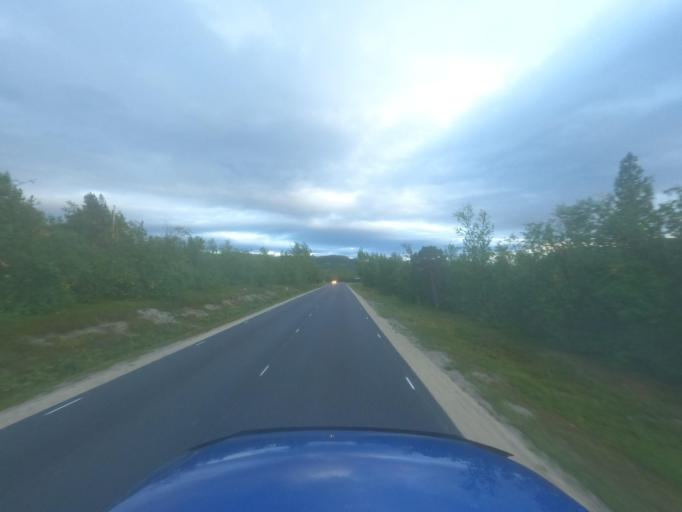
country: NO
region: Finnmark Fylke
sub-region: Porsanger
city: Lakselv
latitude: 69.9768
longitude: 24.9637
